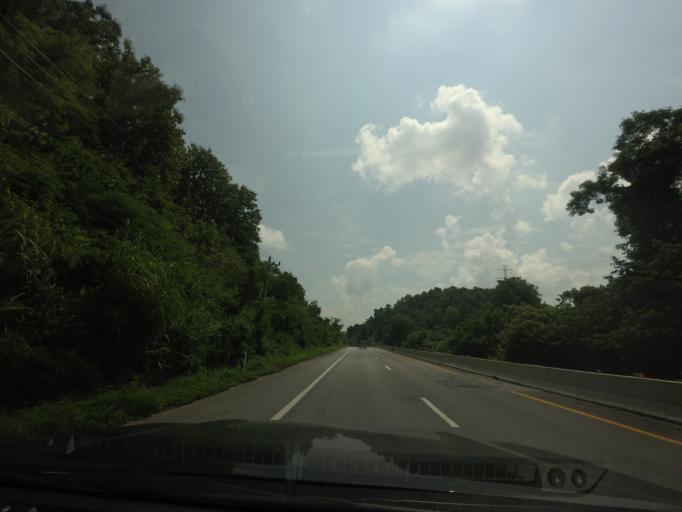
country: TH
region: Uttaradit
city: Lap Lae
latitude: 17.7790
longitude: 100.1227
